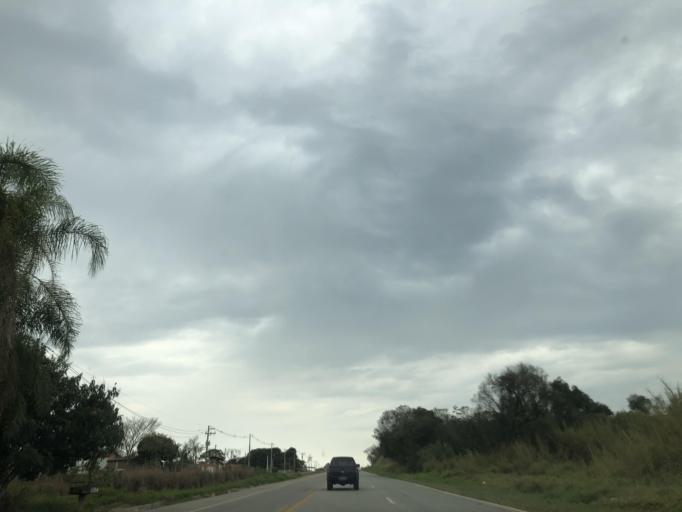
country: BR
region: Sao Paulo
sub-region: Salto De Pirapora
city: Salto de Pirapora
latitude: -23.7054
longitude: -47.6289
